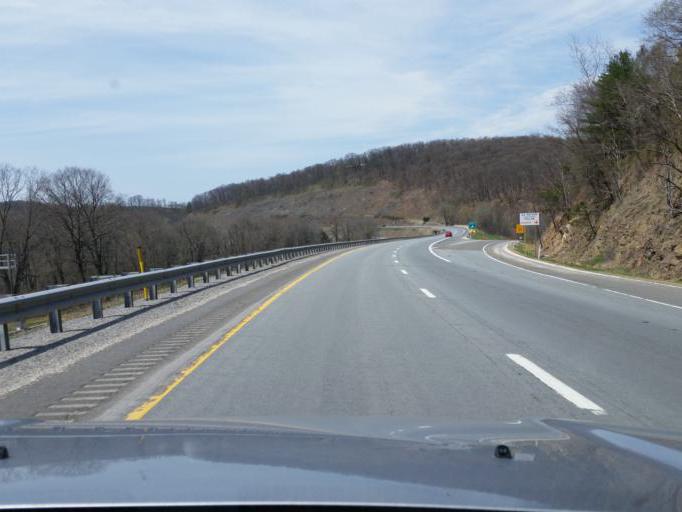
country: US
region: Pennsylvania
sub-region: Perry County
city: Duncannon
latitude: 40.4780
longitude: -77.0436
